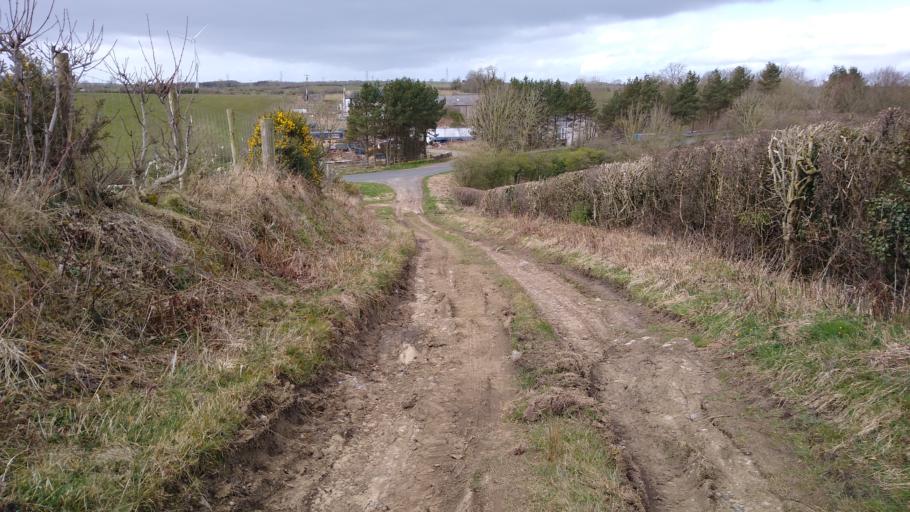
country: GB
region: England
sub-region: Cumbria
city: Dearham
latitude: 54.6925
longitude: -3.4278
